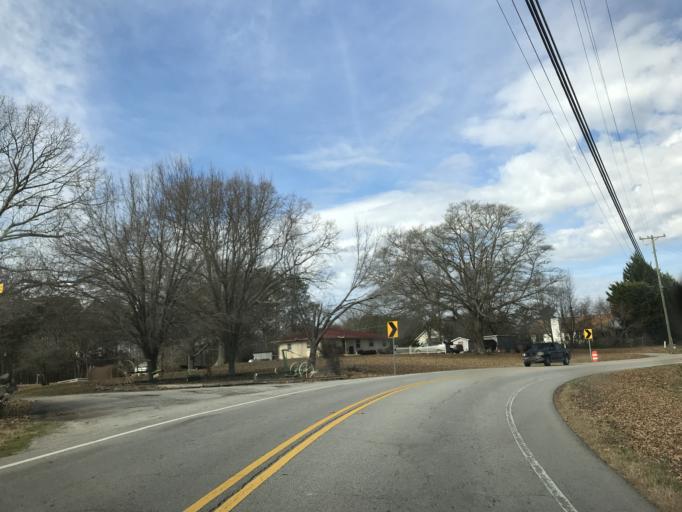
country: US
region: Georgia
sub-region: Carroll County
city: Villa Rica
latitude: 33.8023
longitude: -84.8405
